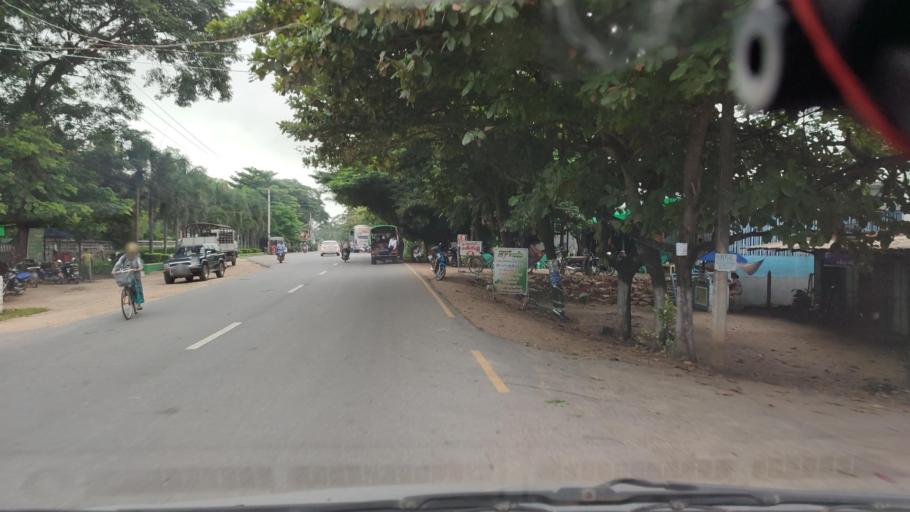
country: MM
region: Bago
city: Pyay
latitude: 18.7008
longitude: 95.2148
